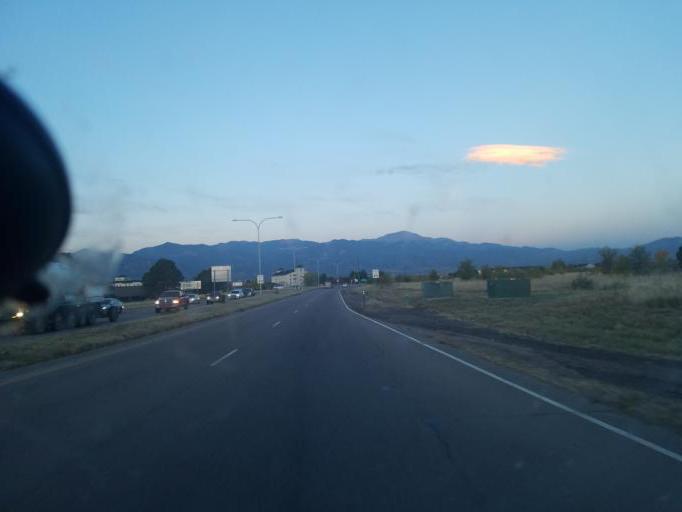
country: US
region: Colorado
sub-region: El Paso County
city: Stratmoor
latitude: 38.8063
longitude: -104.7316
